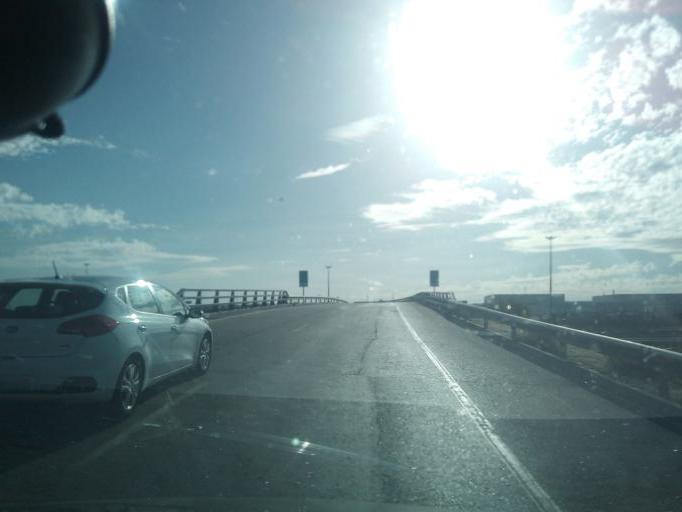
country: ES
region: Madrid
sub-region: Provincia de Madrid
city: Pinto
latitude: 40.2790
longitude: -3.6885
